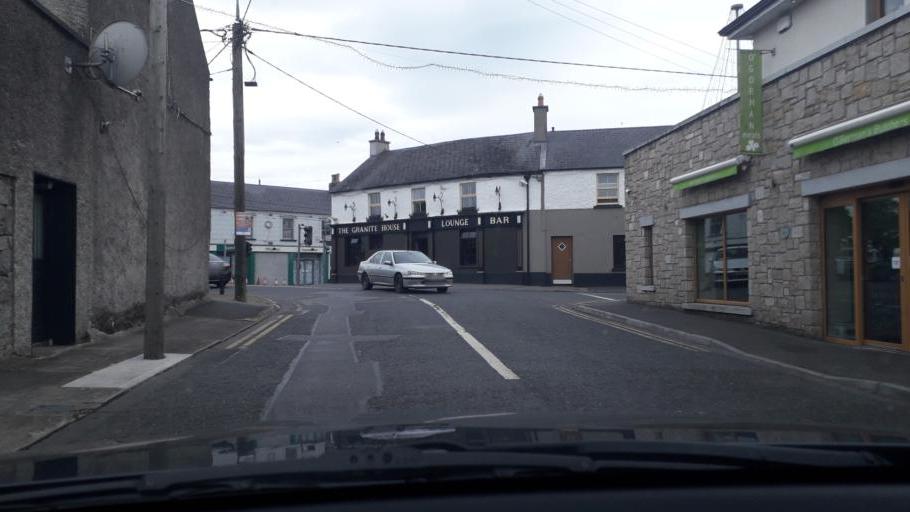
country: IE
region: Leinster
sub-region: Kildare
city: Castledermot
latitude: 52.9121
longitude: -6.8383
